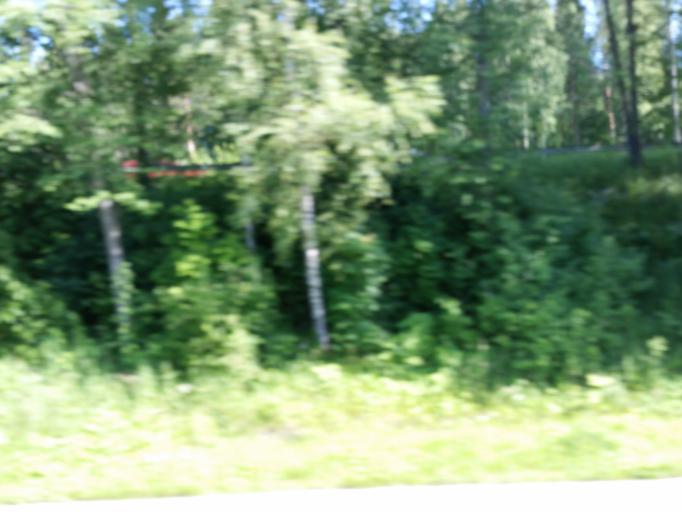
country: FI
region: Northern Savo
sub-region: Kuopio
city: Kuopio
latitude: 62.8960
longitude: 27.6500
